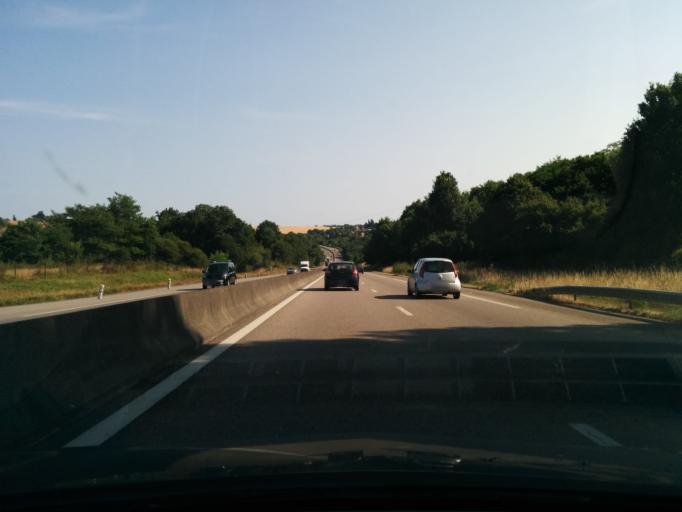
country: FR
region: Limousin
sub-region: Departement de la Haute-Vienne
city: Boisseuil
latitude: 45.7380
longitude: 1.3404
